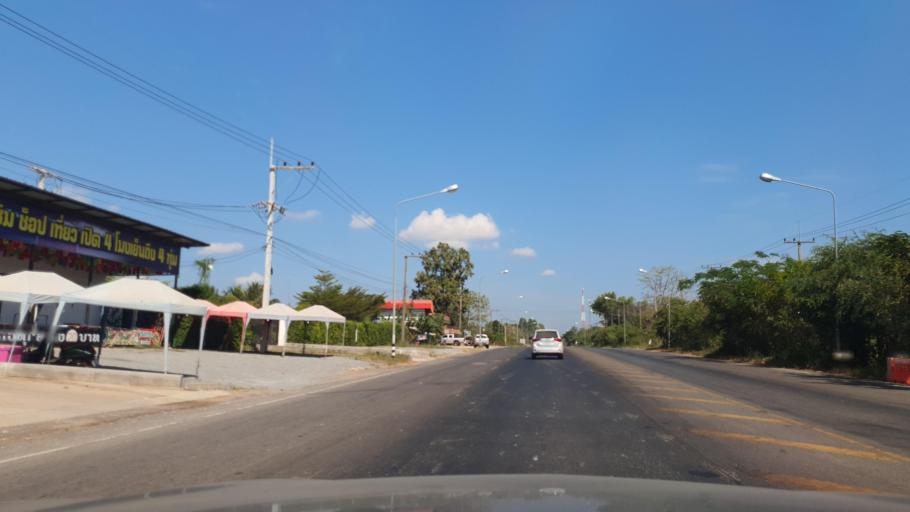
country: TH
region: Kalasin
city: Somdet
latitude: 16.7173
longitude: 103.7561
